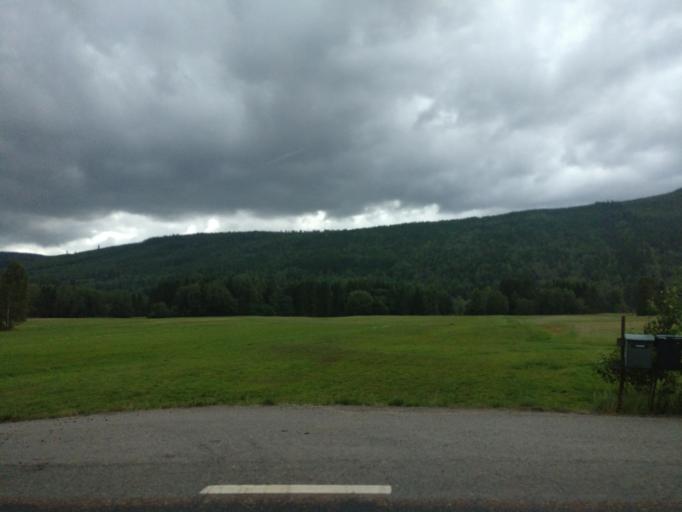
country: SE
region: Vaermland
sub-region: Torsby Kommun
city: Torsby
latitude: 60.7037
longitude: 12.9012
